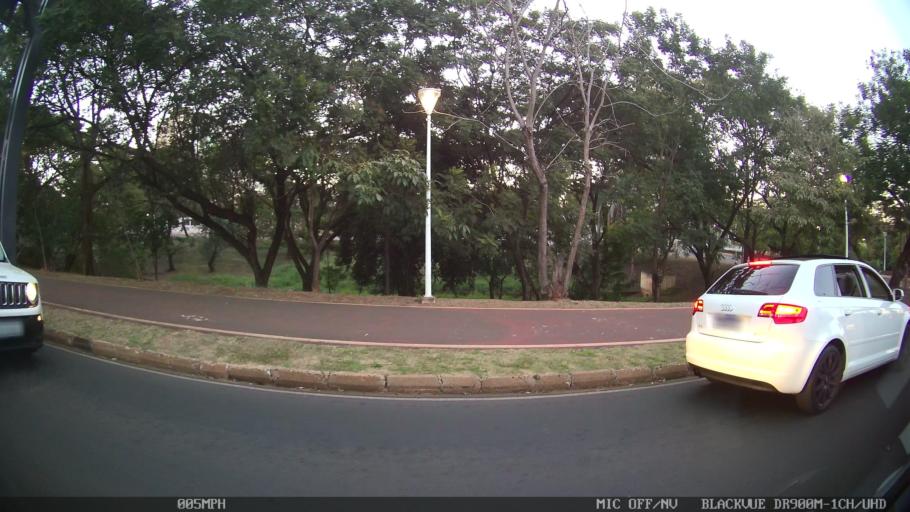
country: BR
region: Sao Paulo
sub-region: Sao Jose Do Rio Preto
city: Sao Jose do Rio Preto
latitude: -20.8299
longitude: -49.3900
